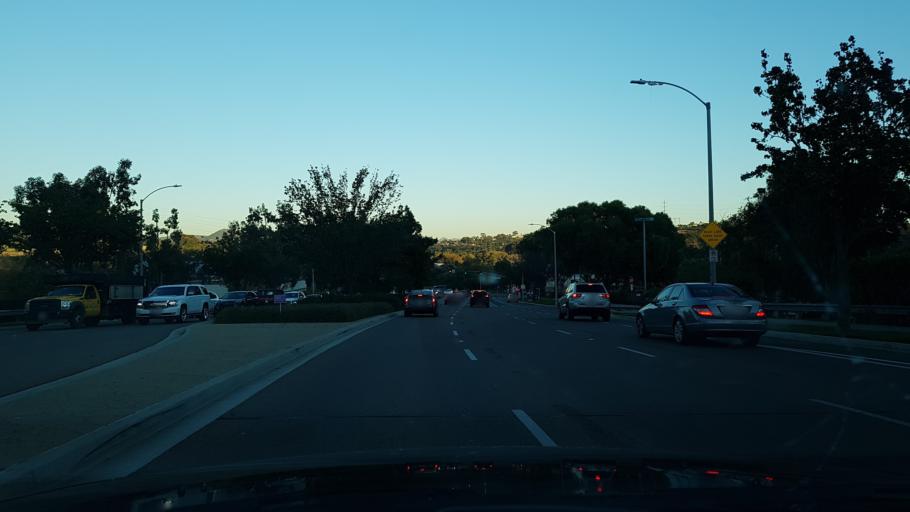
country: US
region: California
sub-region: San Diego County
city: Encinitas
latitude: 33.0684
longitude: -117.2672
